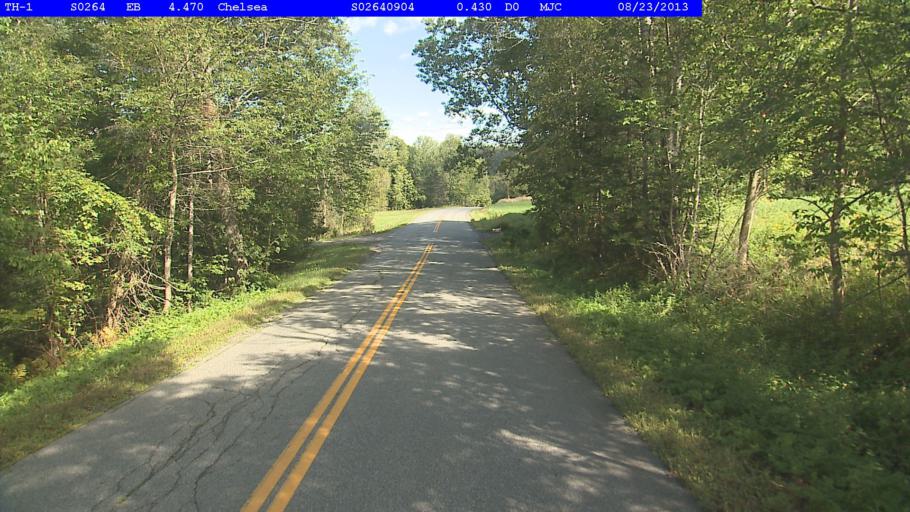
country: US
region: Vermont
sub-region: Orange County
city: Chelsea
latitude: 43.9728
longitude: -72.5040
